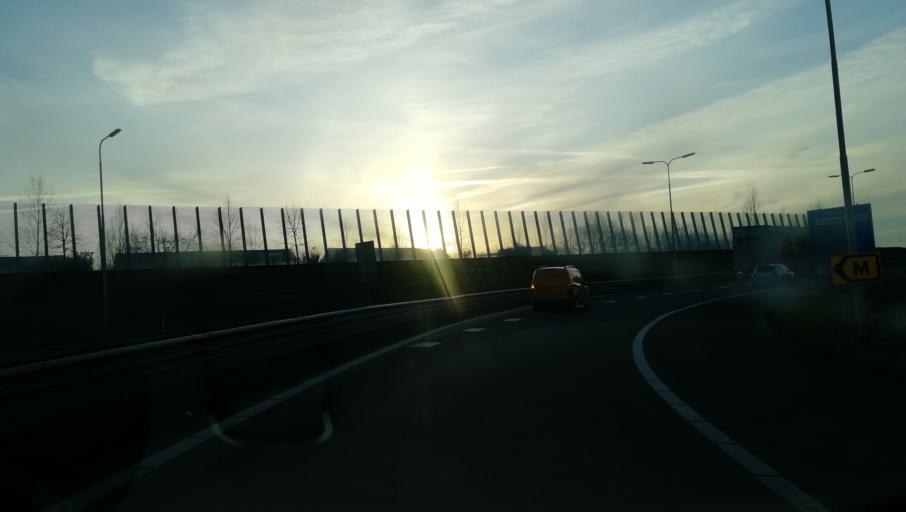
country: NL
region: Limburg
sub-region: Gemeente Venlo
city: Tegelen
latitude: 51.3629
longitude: 6.1263
